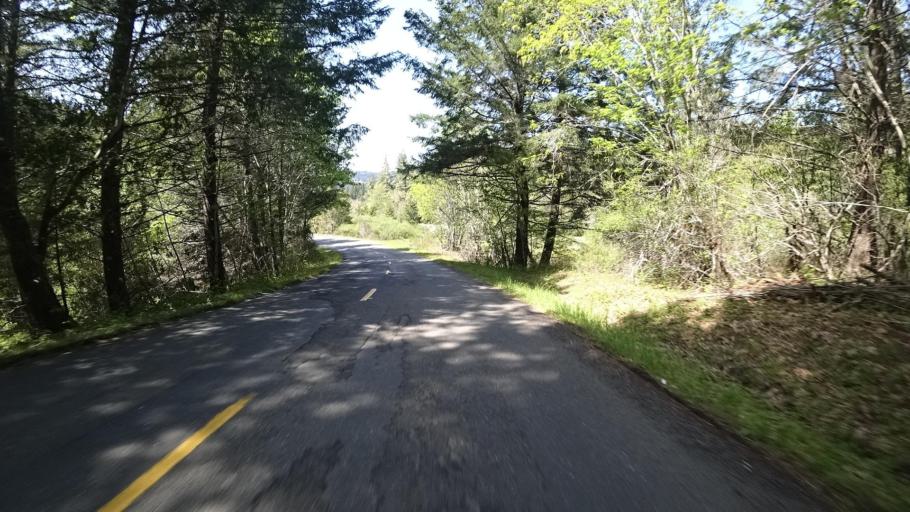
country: US
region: California
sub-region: Humboldt County
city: Redway
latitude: 40.3179
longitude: -123.6605
